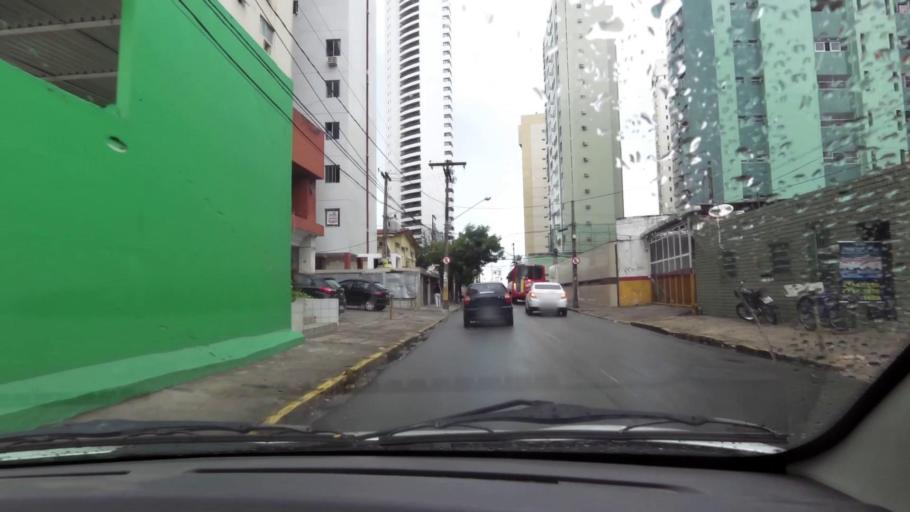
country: BR
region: Pernambuco
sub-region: Recife
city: Recife
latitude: -8.1329
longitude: -34.9025
